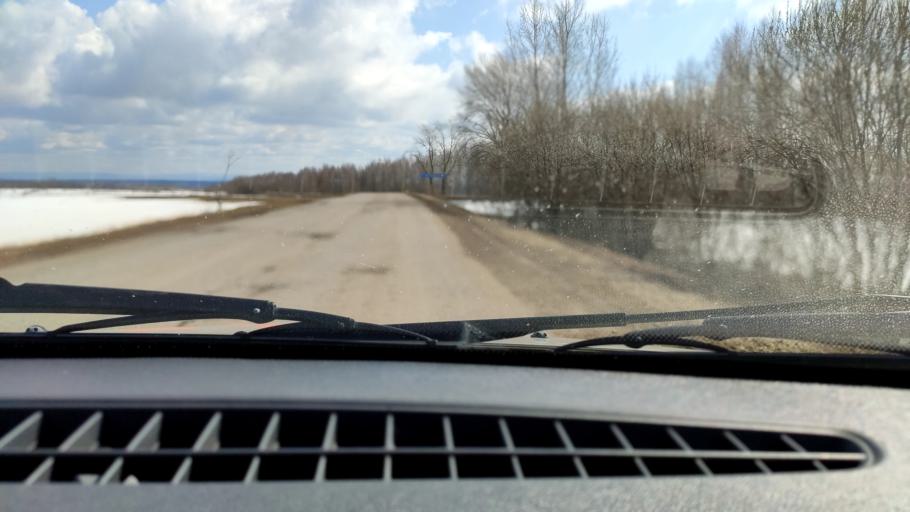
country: RU
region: Bashkortostan
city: Kudeyevskiy
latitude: 54.8635
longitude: 56.7535
